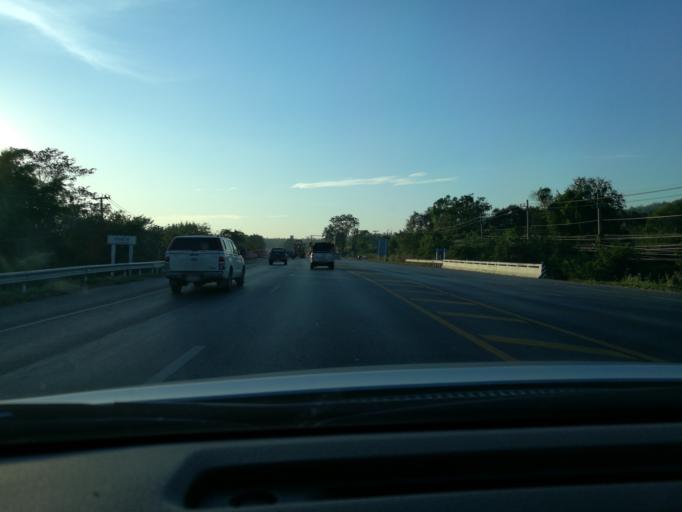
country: TH
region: Phitsanulok
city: Wang Thong
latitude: 16.8426
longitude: 100.5484
